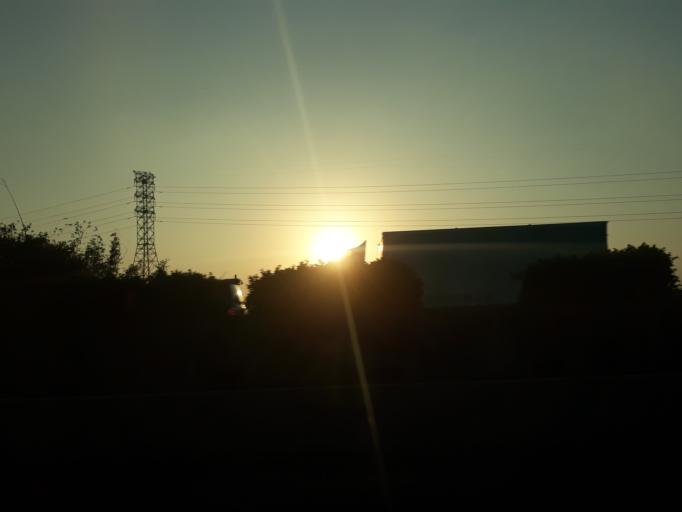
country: TW
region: Taiwan
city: Fengshan
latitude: 22.7771
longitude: 120.3246
